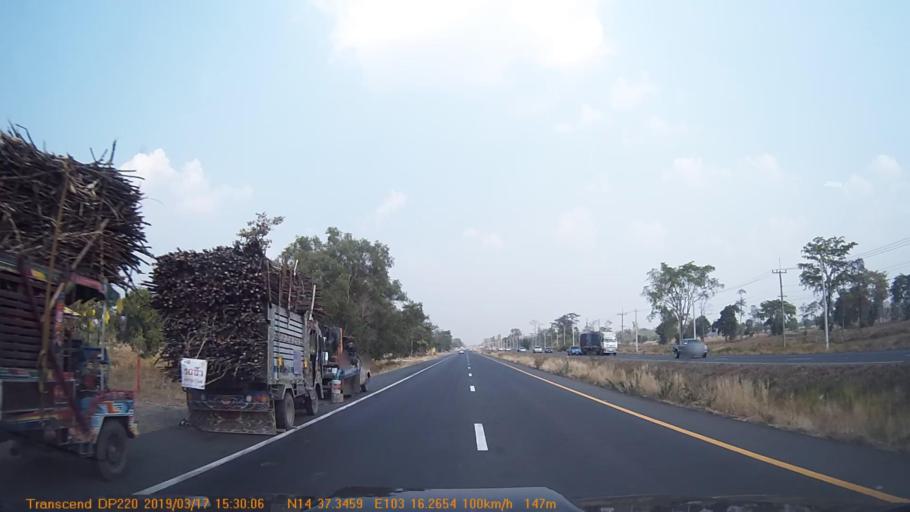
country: TH
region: Surin
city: Prasat
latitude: 14.6223
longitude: 103.2715
